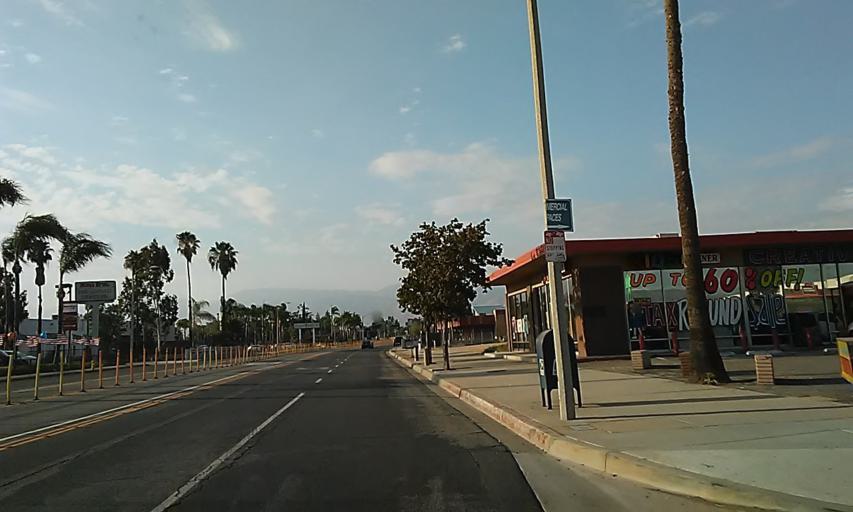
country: US
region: California
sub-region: San Bernardino County
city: Colton
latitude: 34.0811
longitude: -117.2941
